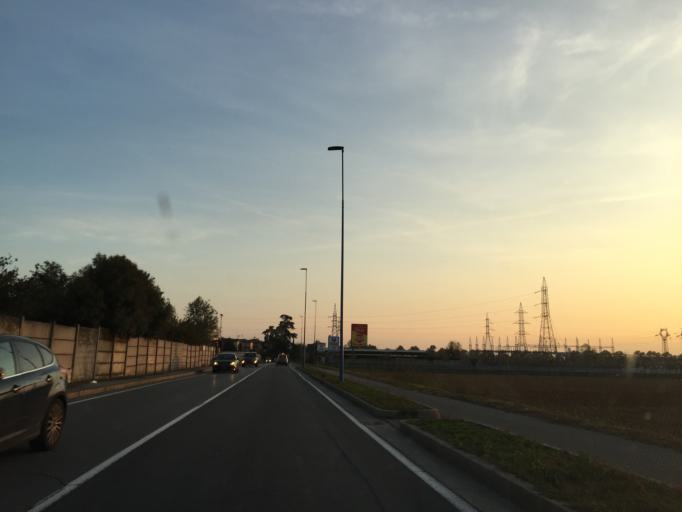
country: IT
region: Lombardy
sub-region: Provincia di Brescia
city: Folzano
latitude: 45.5040
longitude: 10.2145
